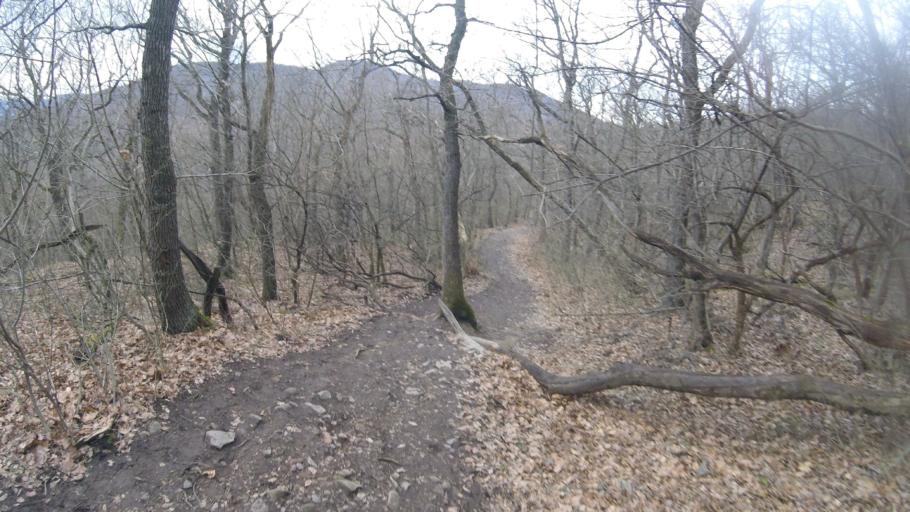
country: HU
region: Pest
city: Nagykovacsi
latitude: 47.6741
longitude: 19.0134
